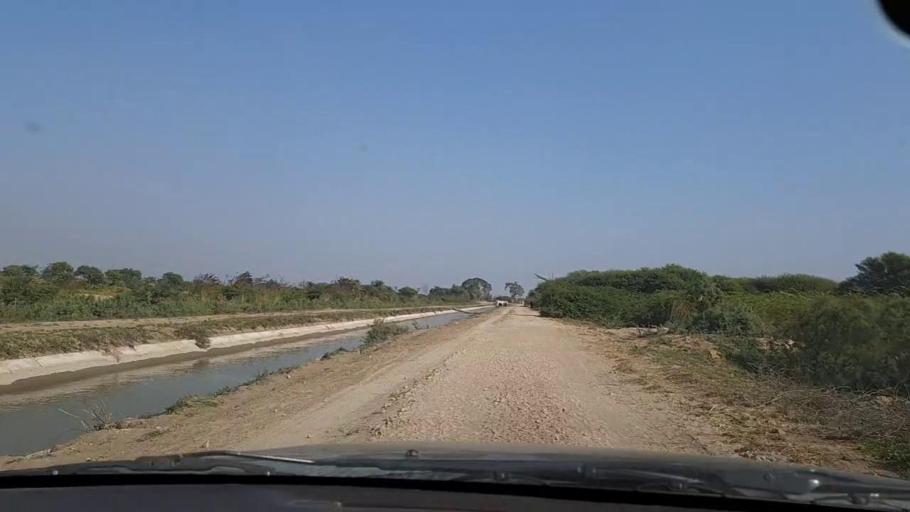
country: PK
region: Sindh
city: Mirpur Sakro
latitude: 24.3421
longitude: 67.7296
